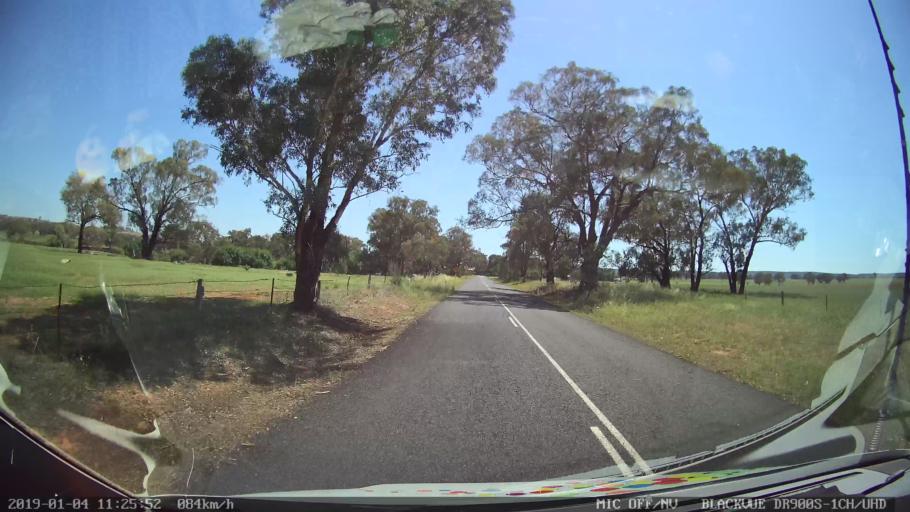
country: AU
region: New South Wales
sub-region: Cabonne
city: Molong
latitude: -33.1196
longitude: 148.7535
